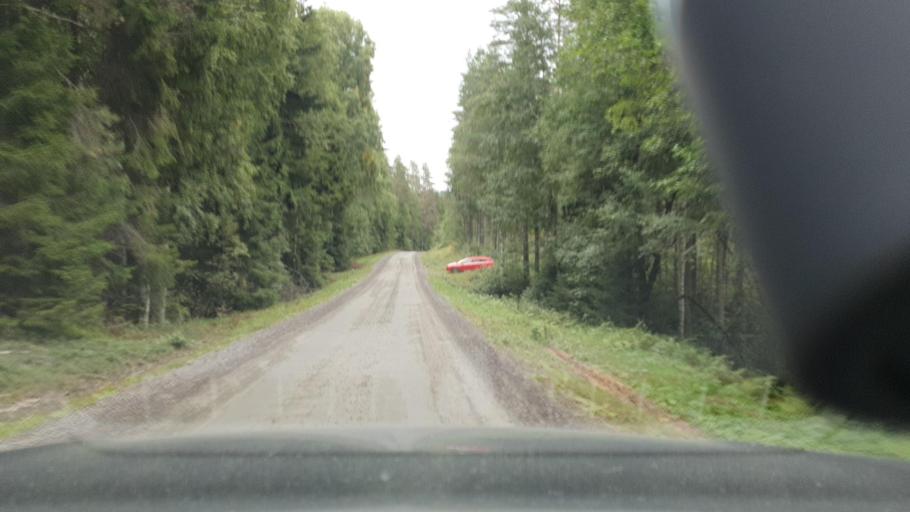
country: SE
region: Vaermland
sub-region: Torsby Kommun
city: Torsby
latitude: 60.3844
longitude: 12.8905
